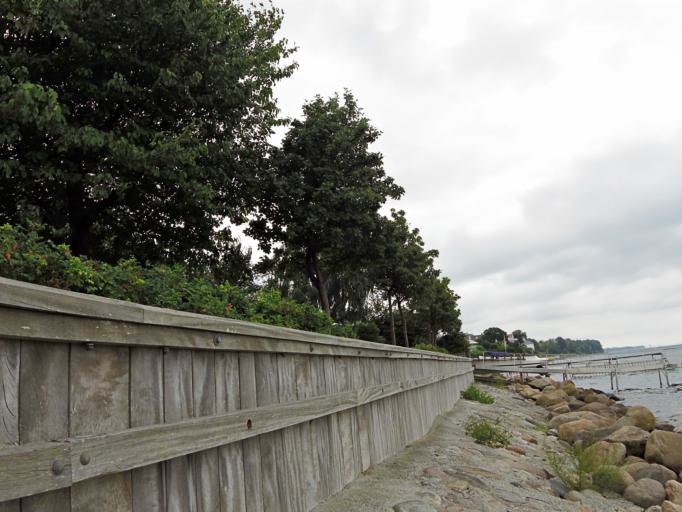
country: DK
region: Capital Region
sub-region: Gentofte Kommune
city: Charlottenlund
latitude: 55.7903
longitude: 12.5940
